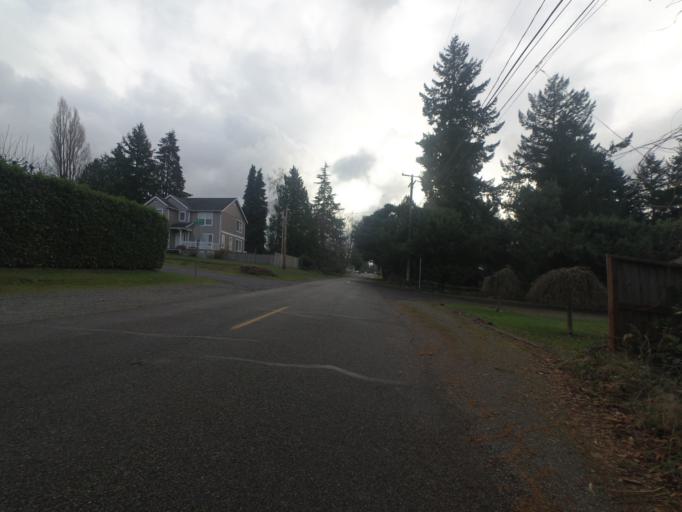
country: US
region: Washington
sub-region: Pierce County
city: University Place
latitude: 47.2411
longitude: -122.5424
